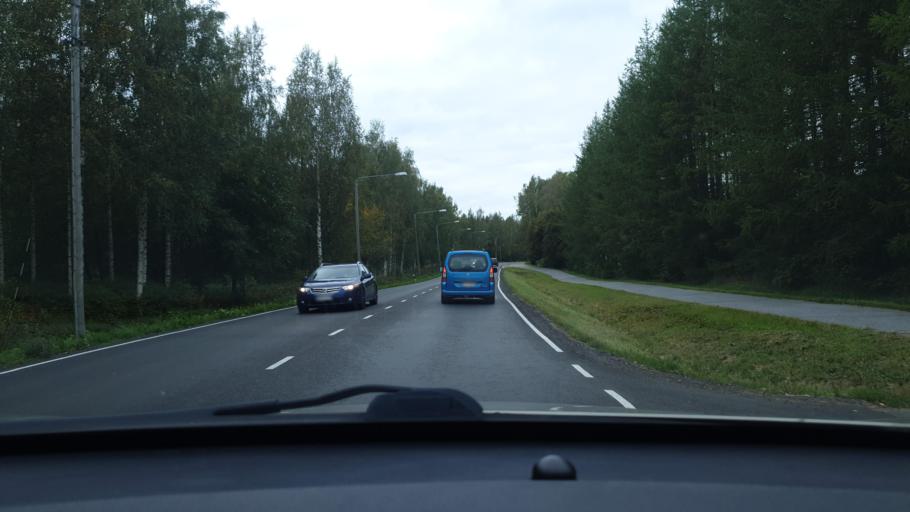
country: FI
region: Ostrobothnia
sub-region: Vaasa
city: Teeriniemi
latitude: 63.0869
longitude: 21.6955
